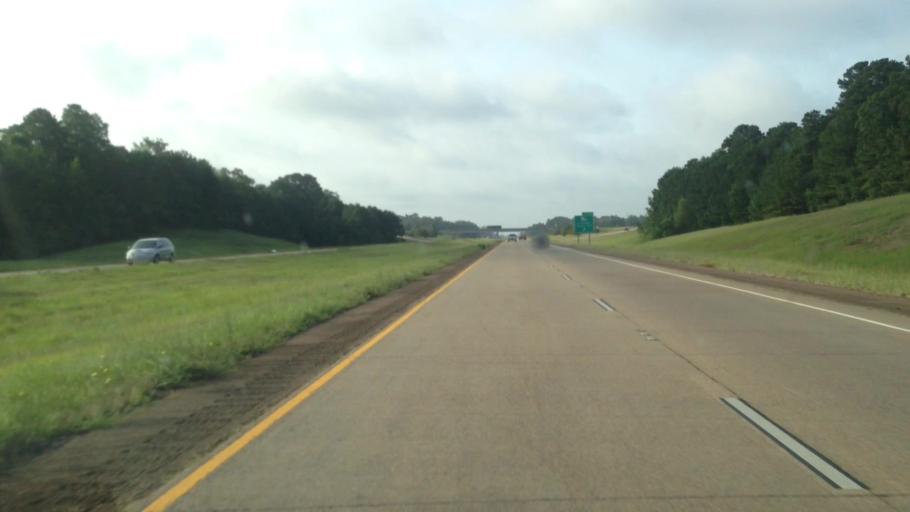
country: US
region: Louisiana
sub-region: Rapides Parish
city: Lecompte
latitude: 31.0782
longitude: -92.4374
